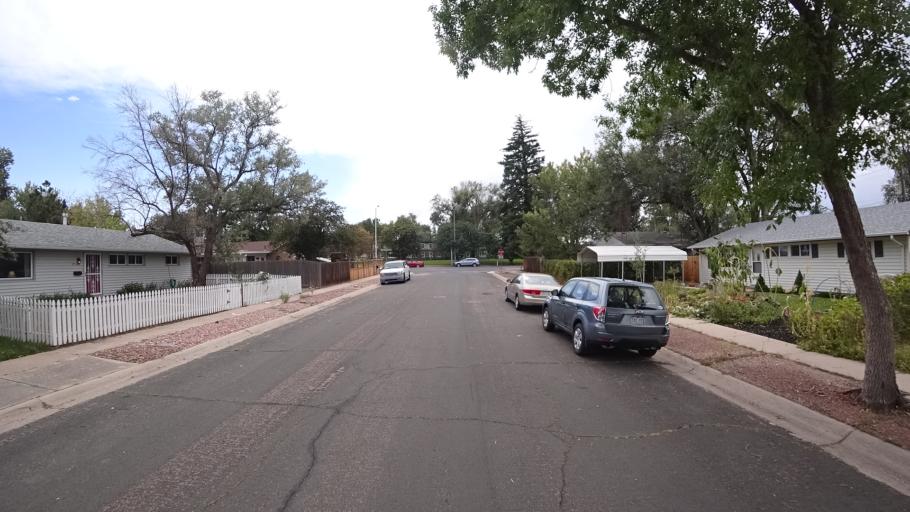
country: US
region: Colorado
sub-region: El Paso County
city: Colorado Springs
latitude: 38.8685
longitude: -104.7909
